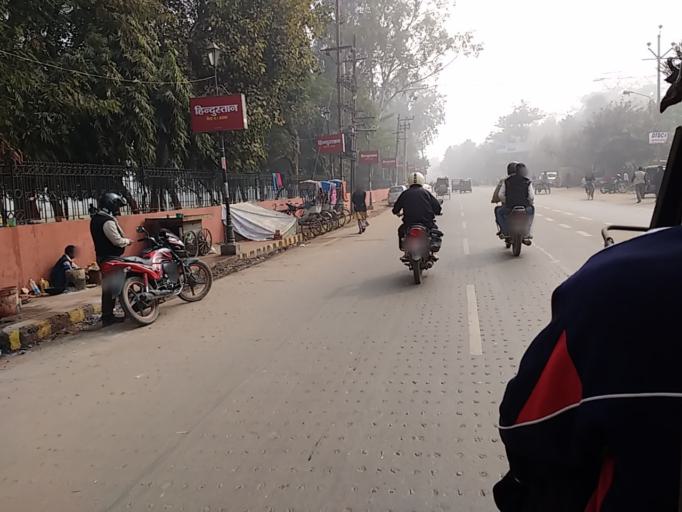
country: IN
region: Bihar
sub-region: Patna
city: Patna
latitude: 25.6153
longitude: 85.1450
